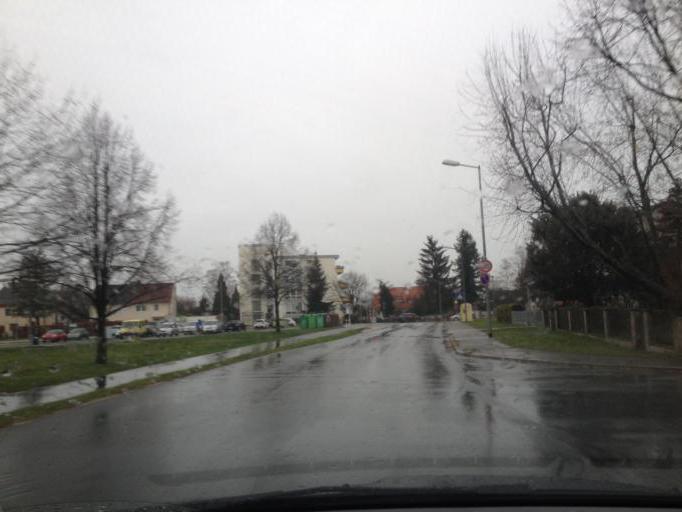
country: DE
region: Bavaria
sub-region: Regierungsbezirk Mittelfranken
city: Lauf an der Pegnitz
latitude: 49.5155
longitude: 11.2762
